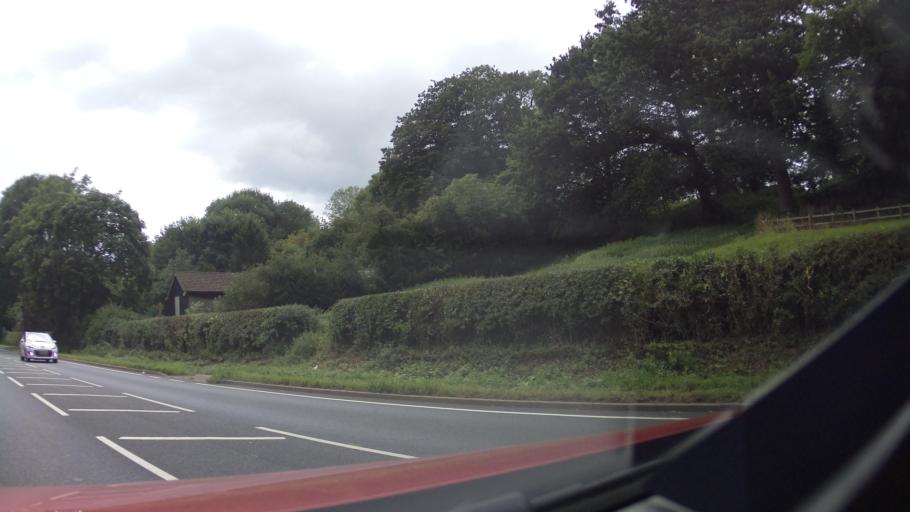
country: GB
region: England
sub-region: Nottinghamshire
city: Burton Joyce
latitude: 52.9961
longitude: -1.0227
